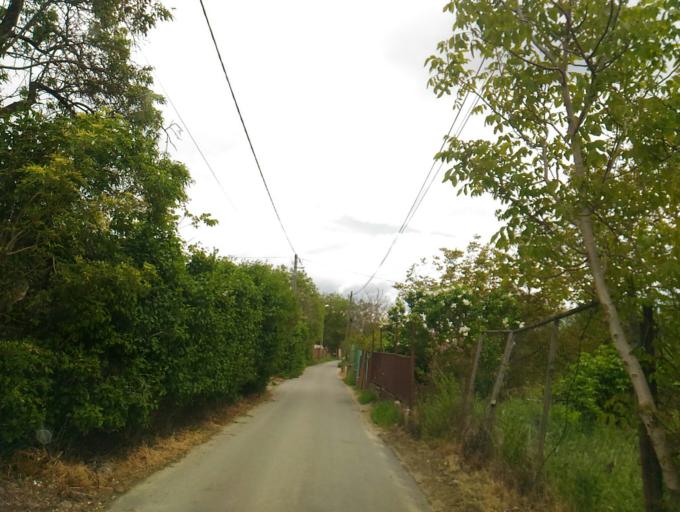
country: HU
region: Pest
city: Diosd
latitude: 47.3990
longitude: 18.9630
